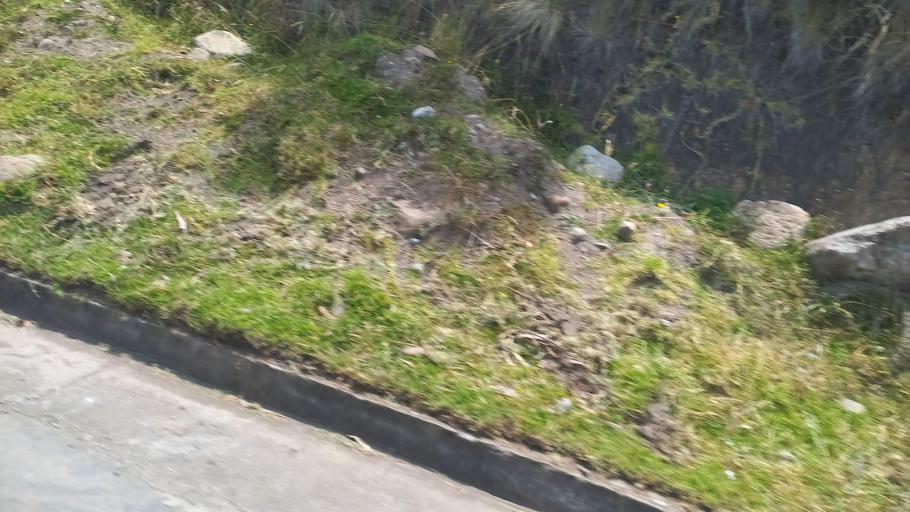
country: EC
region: Pichincha
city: Cayambe
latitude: 0.1784
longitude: -78.0918
